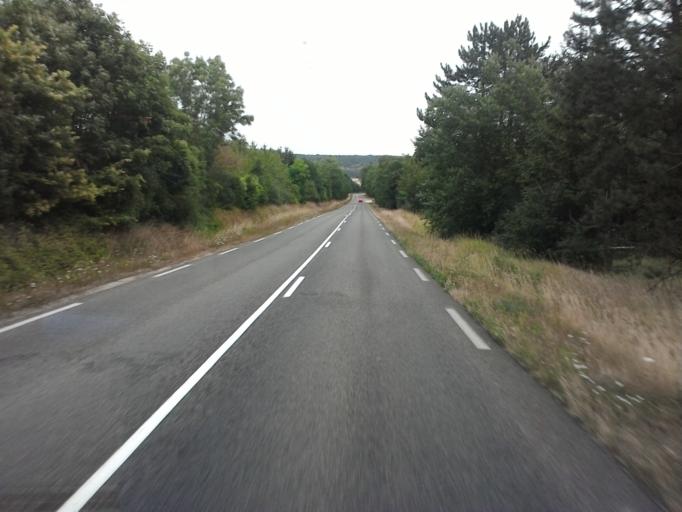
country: FR
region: Lorraine
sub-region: Departement de Meurthe-et-Moselle
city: Chaligny
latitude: 48.5789
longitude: 6.0064
